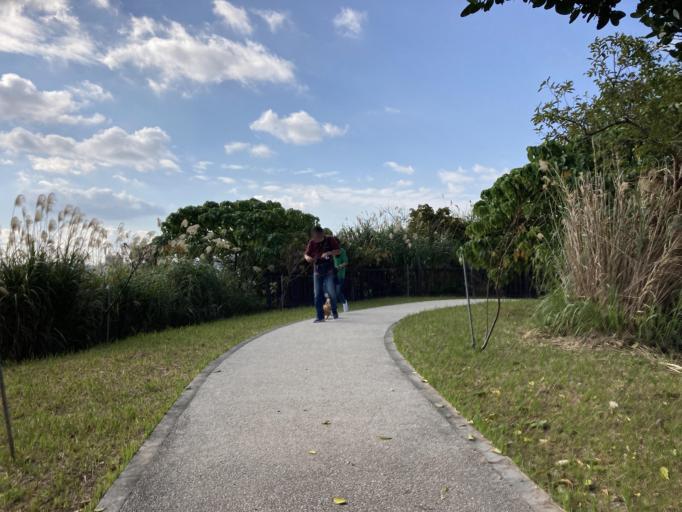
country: JP
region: Okinawa
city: Naha-shi
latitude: 26.2029
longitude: 127.6764
